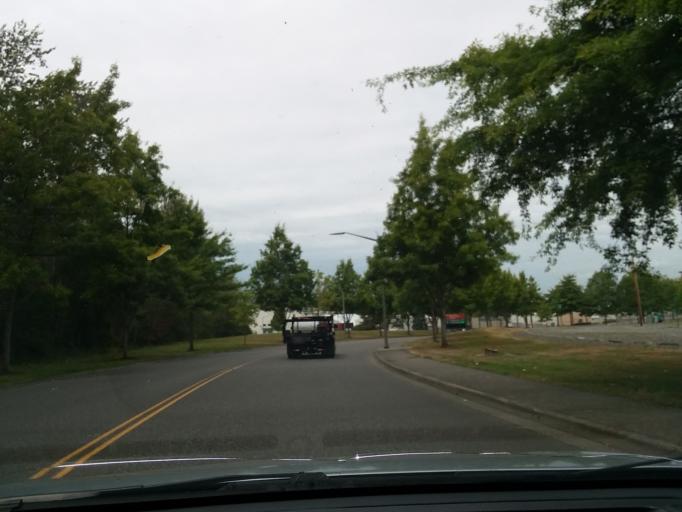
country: US
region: Washington
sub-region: Whatcom County
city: Marietta-Alderwood
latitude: 48.7883
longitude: -122.5297
